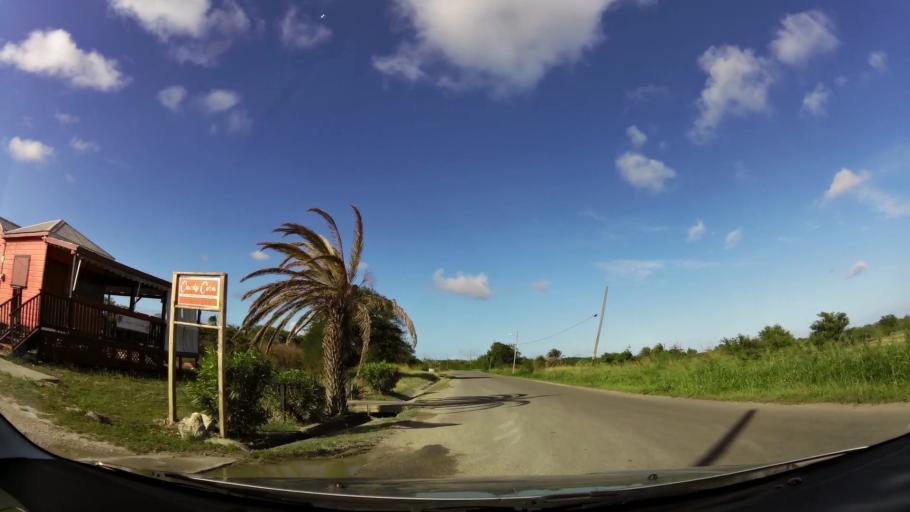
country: AG
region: Saint George
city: Piggotts
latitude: 17.1022
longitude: -61.8007
